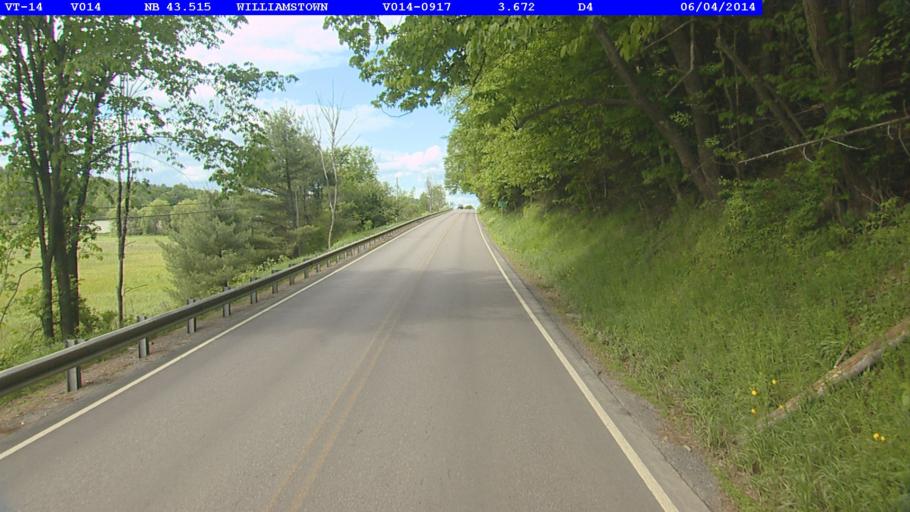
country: US
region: Vermont
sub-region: Orange County
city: Williamstown
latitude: 44.1108
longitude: -72.5403
